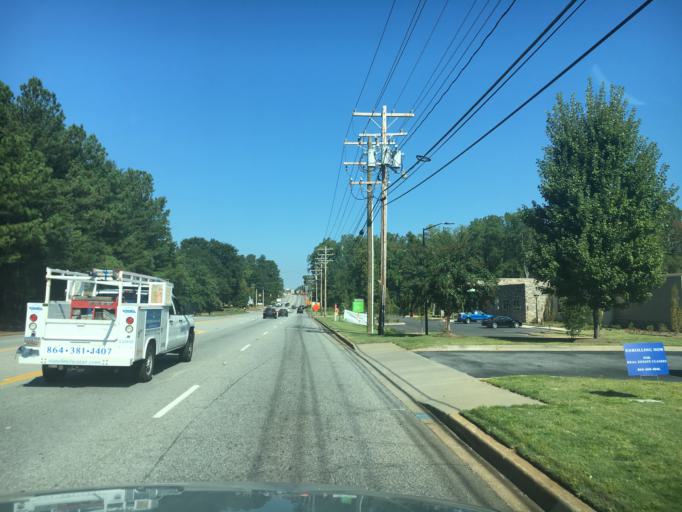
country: US
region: South Carolina
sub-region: Spartanburg County
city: Valley Falls
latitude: 35.0261
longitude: -81.9651
